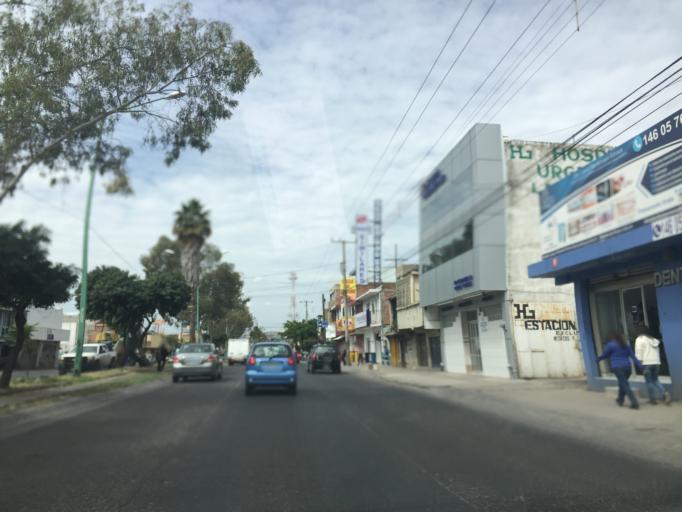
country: MX
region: Guanajuato
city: Leon
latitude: 21.1024
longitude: -101.6859
